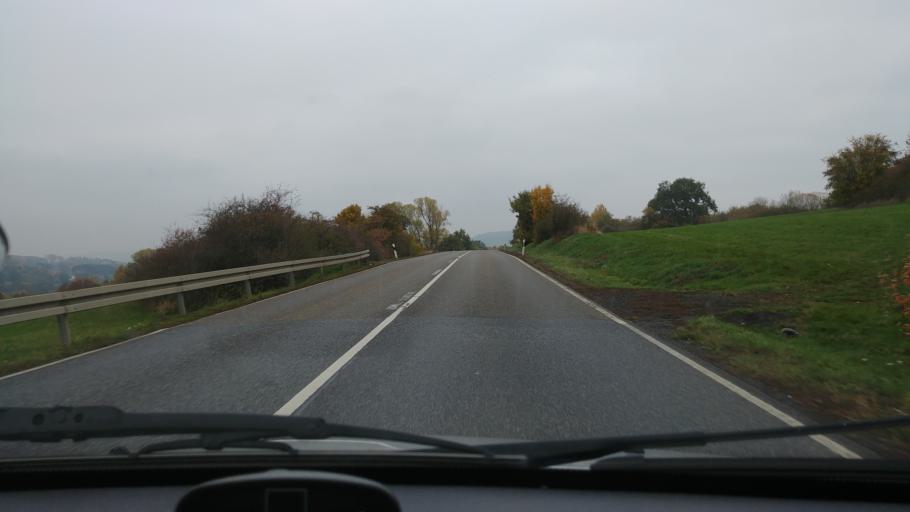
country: DE
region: Rheinland-Pfalz
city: Irmtraut
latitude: 50.5217
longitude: 8.0546
